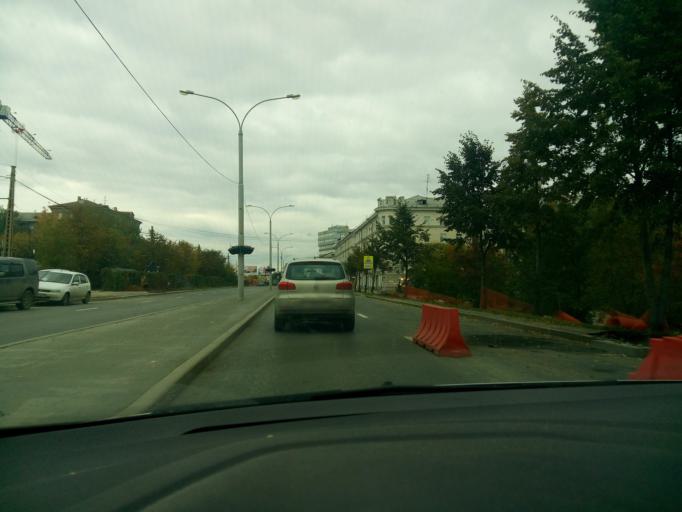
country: RU
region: Sverdlovsk
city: Yekaterinburg
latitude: 56.8389
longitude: 60.5736
